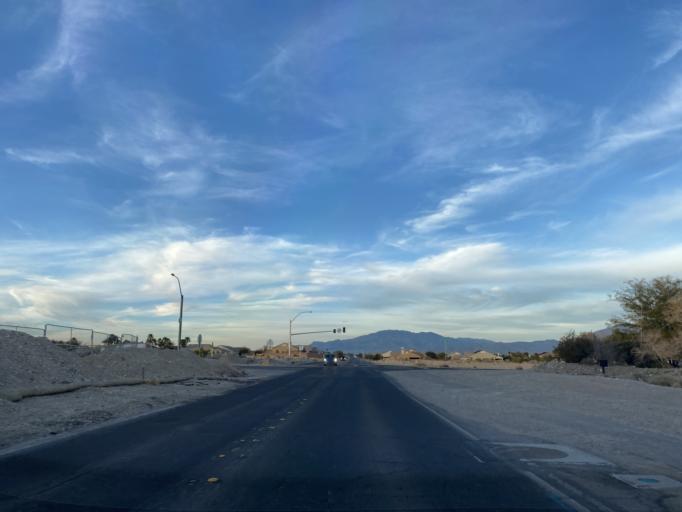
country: US
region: Nevada
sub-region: Clark County
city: Summerlin South
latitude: 36.2695
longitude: -115.2971
